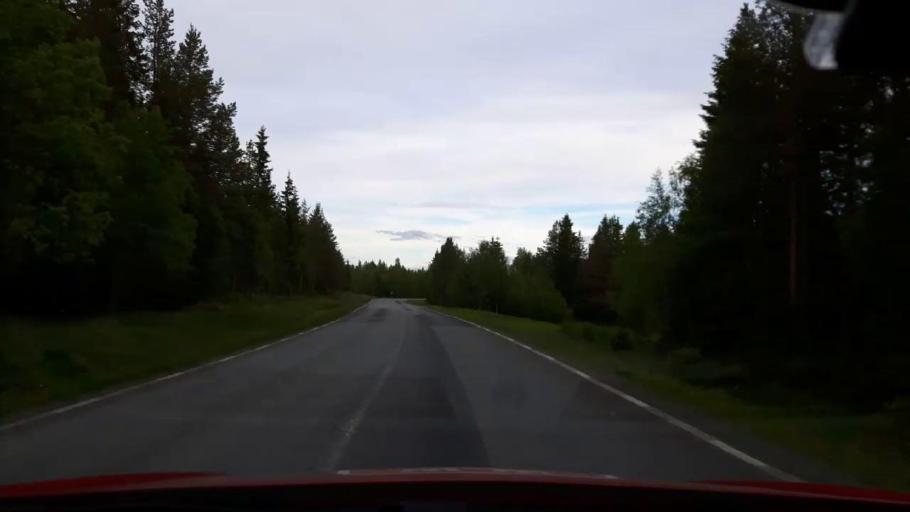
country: SE
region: Jaemtland
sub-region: OEstersunds Kommun
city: Ostersund
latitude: 63.0720
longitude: 14.4453
